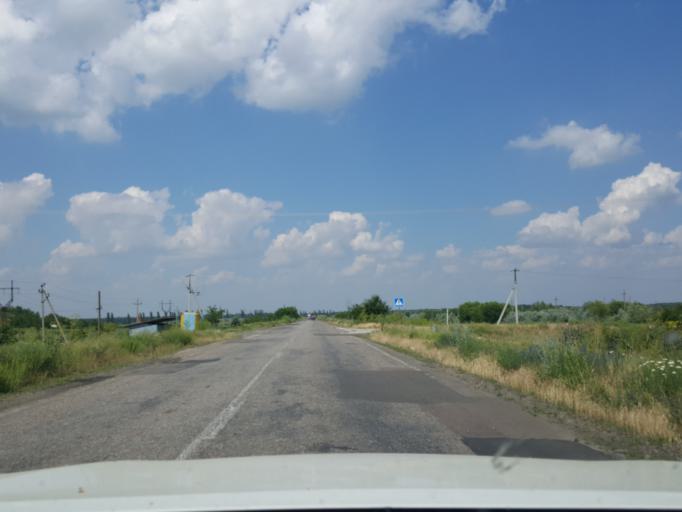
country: UA
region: Odessa
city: Starokozache
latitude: 46.4031
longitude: 30.1020
